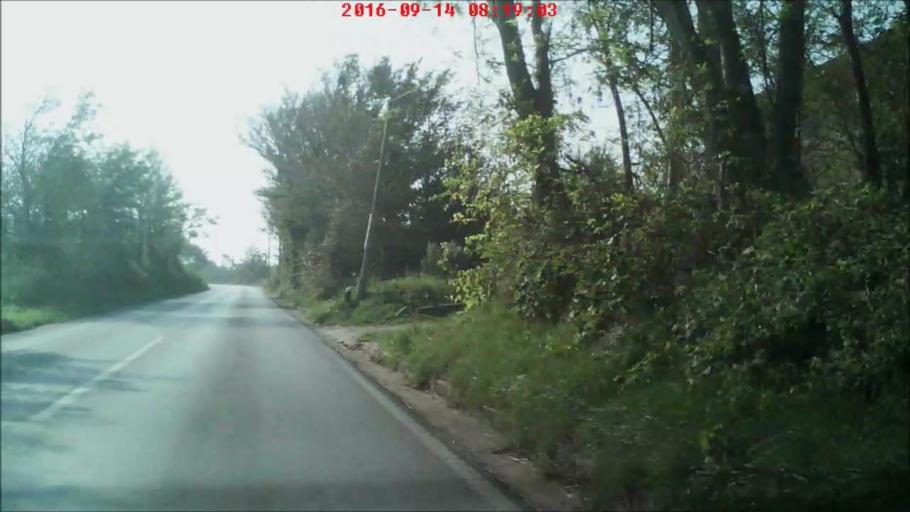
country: HR
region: Zadarska
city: Nin
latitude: 44.2354
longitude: 15.1870
